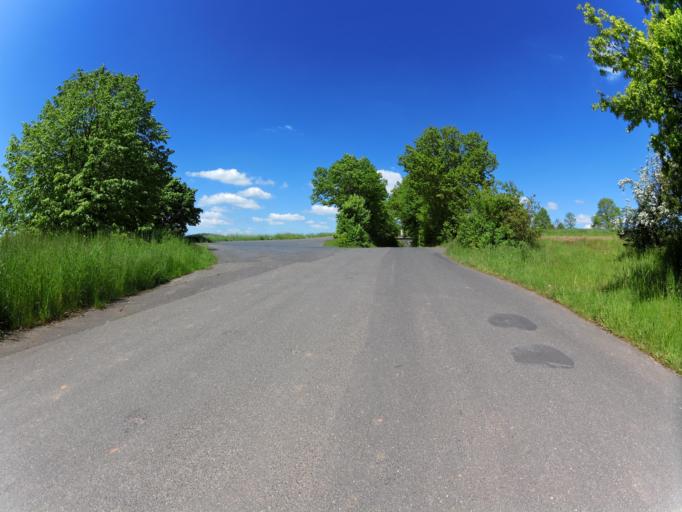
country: DE
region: Thuringia
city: Dankmarshausen
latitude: 50.9581
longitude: 10.0091
